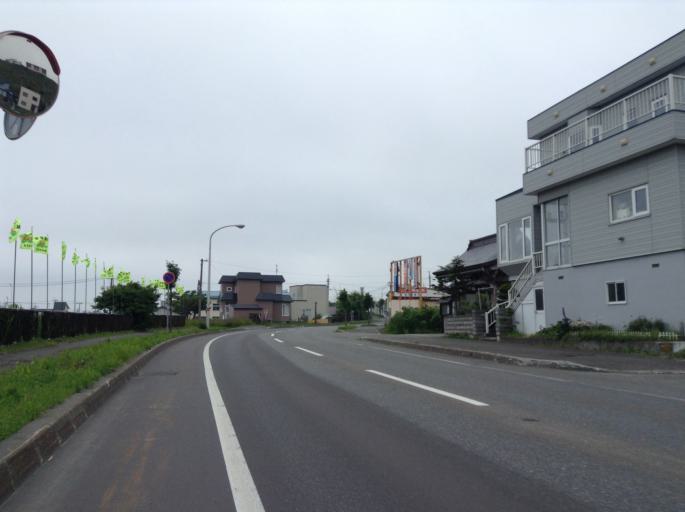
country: JP
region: Hokkaido
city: Wakkanai
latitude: 45.3976
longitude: 141.6834
